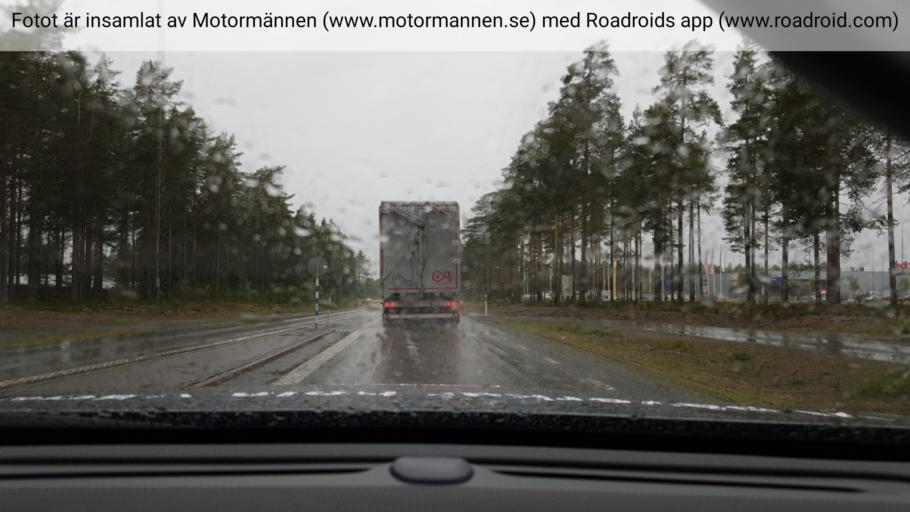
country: SE
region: Vaesterbotten
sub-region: Umea Kommun
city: Roback
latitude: 63.8461
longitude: 20.1602
